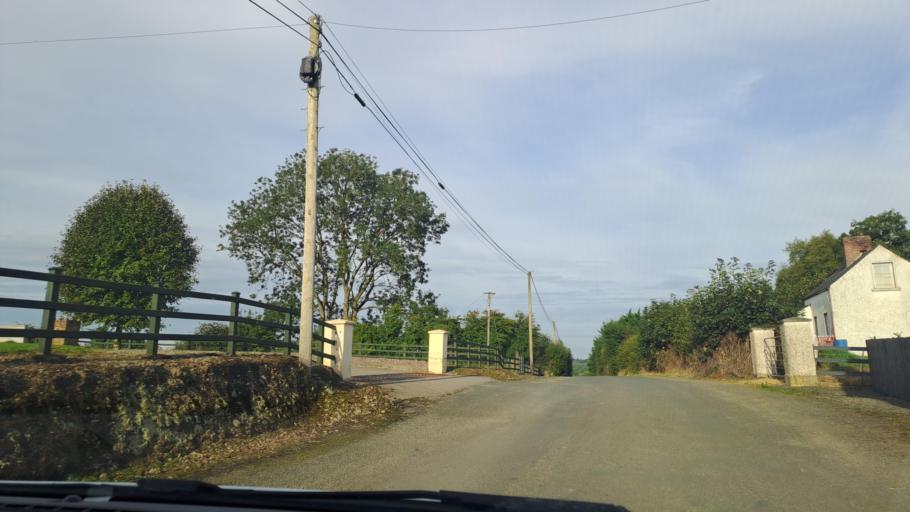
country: IE
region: Ulster
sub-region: An Cabhan
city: Kingscourt
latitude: 53.9890
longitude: -6.8804
